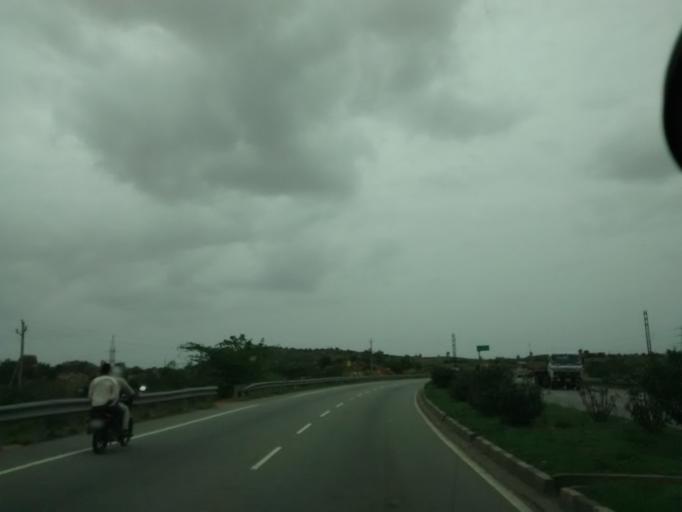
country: IN
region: Andhra Pradesh
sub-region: Kurnool
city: Ramapuram
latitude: 15.2180
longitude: 77.7223
